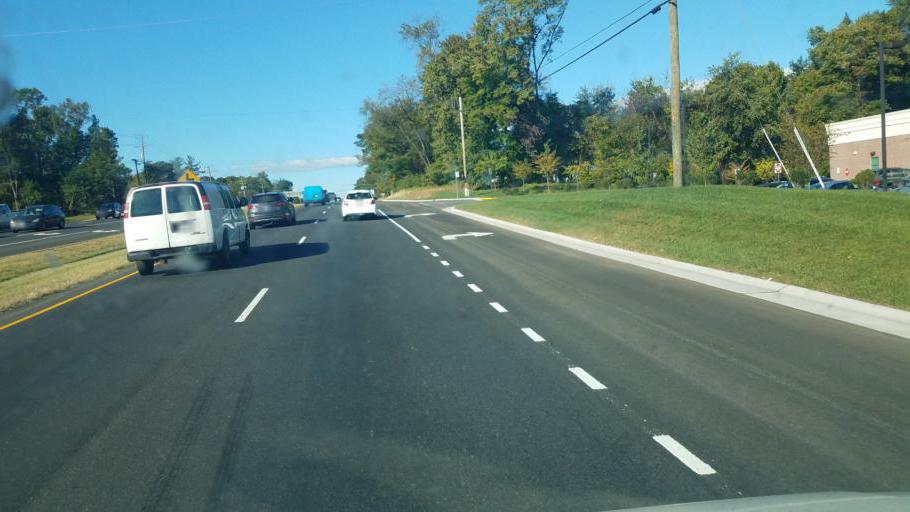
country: US
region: Virginia
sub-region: Prince William County
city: Gainesville
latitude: 38.7913
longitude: -77.6311
